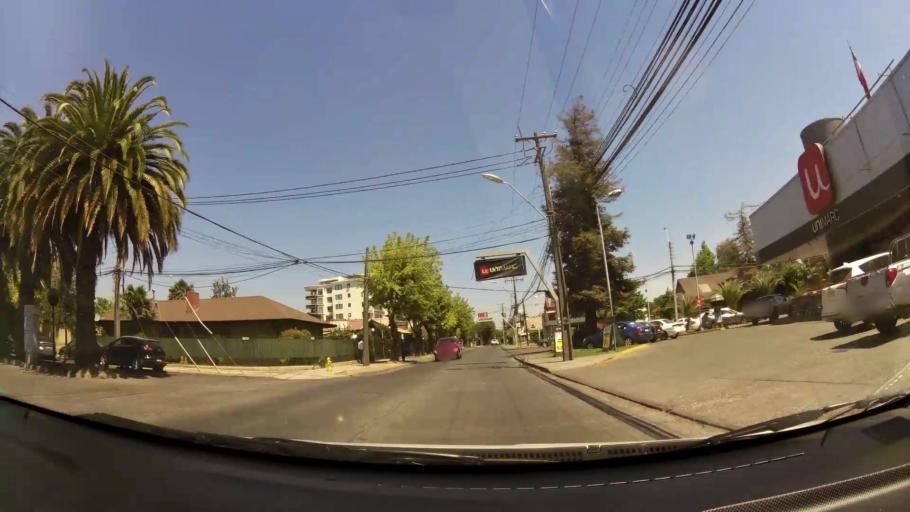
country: CL
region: Maule
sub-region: Provincia de Curico
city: Curico
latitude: -34.9857
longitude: -71.2261
